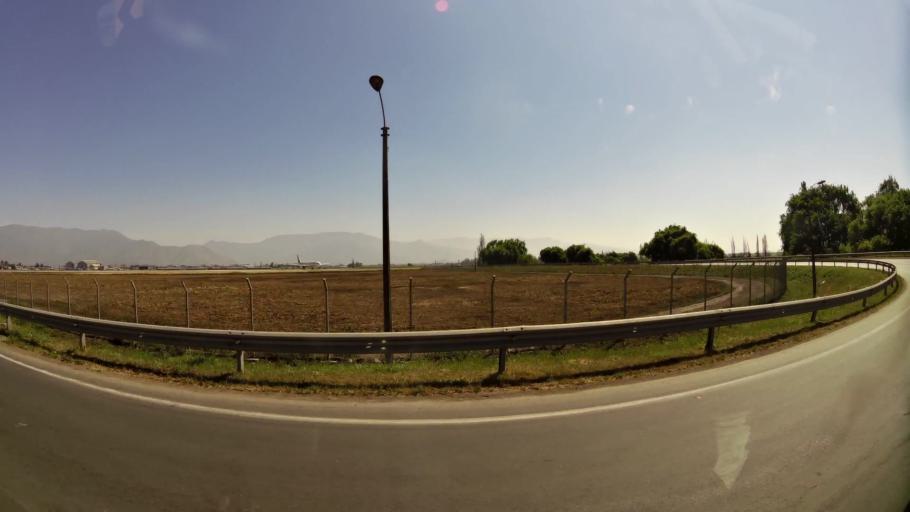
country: CL
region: Santiago Metropolitan
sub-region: Provincia de Santiago
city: Lo Prado
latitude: -33.3773
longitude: -70.7822
